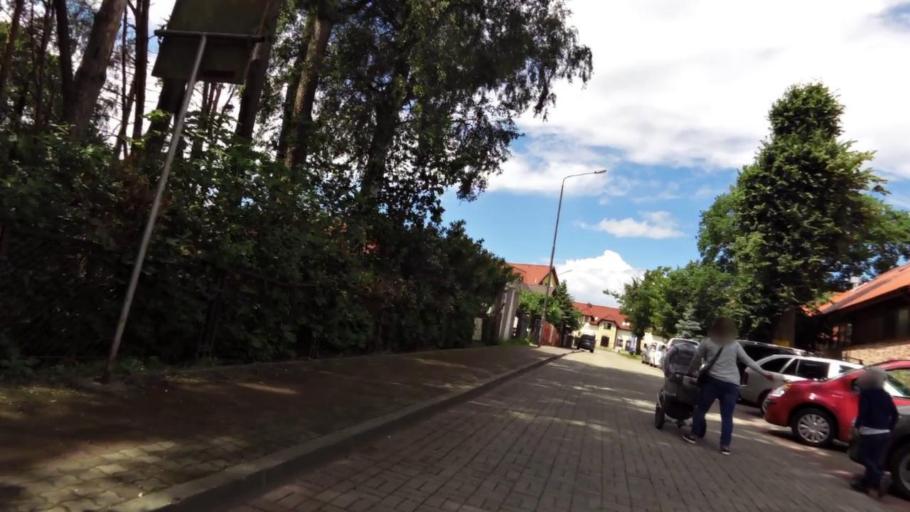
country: PL
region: West Pomeranian Voivodeship
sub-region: Powiat slawienski
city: Darlowo
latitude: 54.5379
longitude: 16.5288
